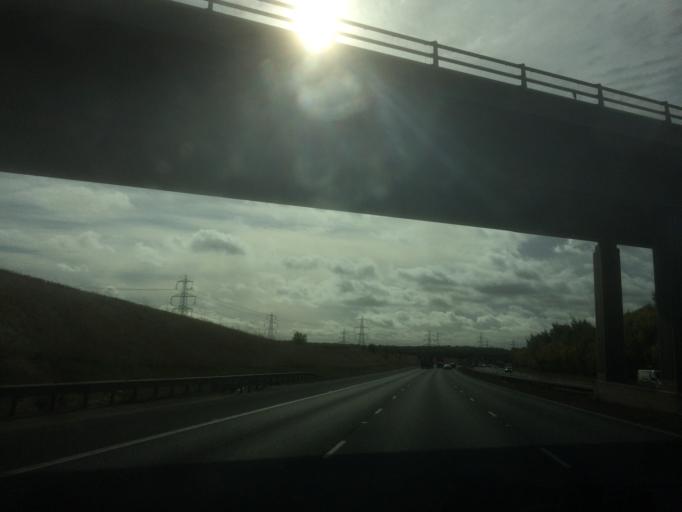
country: GB
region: England
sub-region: North Yorkshire
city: Byram
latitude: 53.7509
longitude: -1.2744
